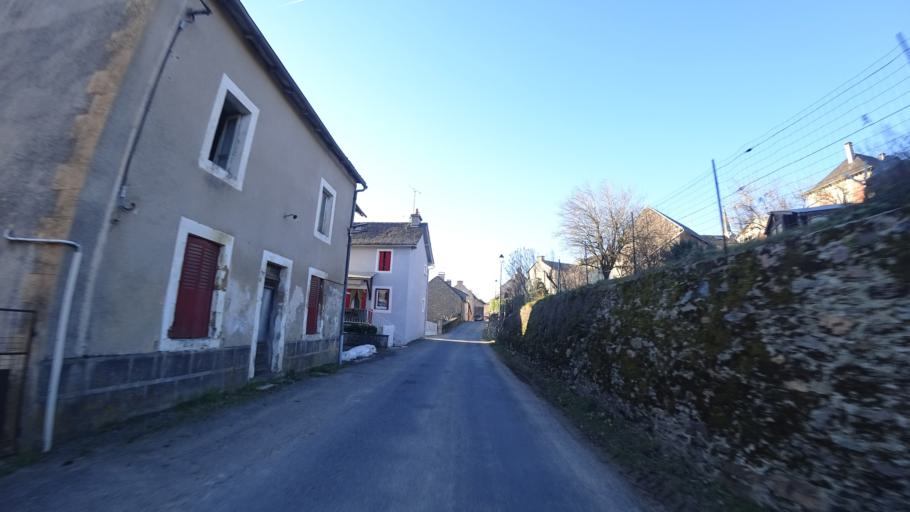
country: FR
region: Midi-Pyrenees
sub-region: Departement de l'Aveyron
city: Pont-de-Salars
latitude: 44.3142
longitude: 2.7558
